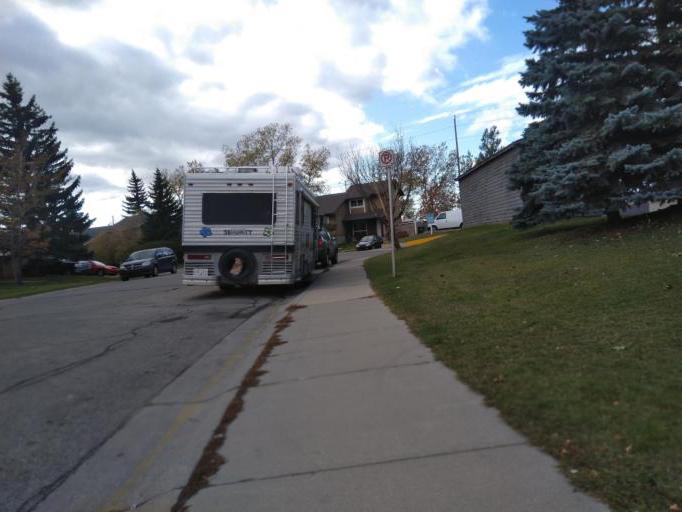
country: CA
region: Alberta
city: Calgary
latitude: 51.0210
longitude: -113.9997
